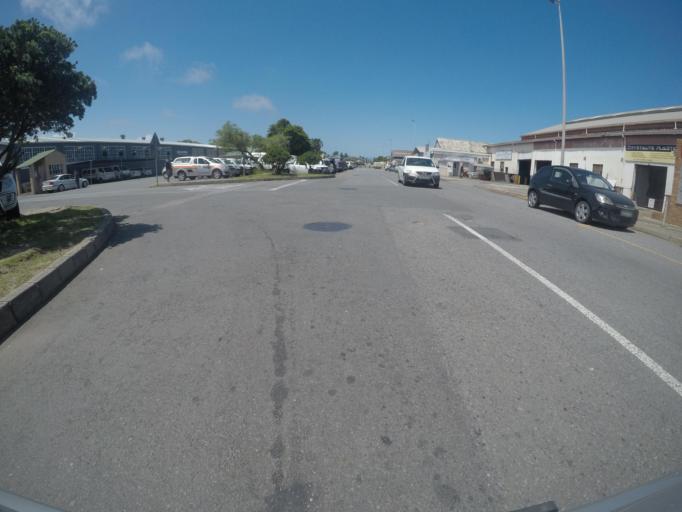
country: ZA
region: Eastern Cape
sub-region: Buffalo City Metropolitan Municipality
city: East London
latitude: -33.0102
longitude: 27.9118
